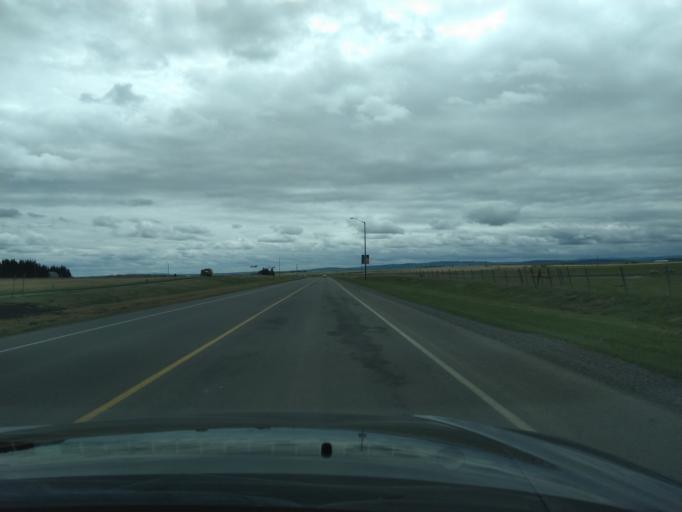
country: CA
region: Alberta
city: Cochrane
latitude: 51.0993
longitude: -114.3887
